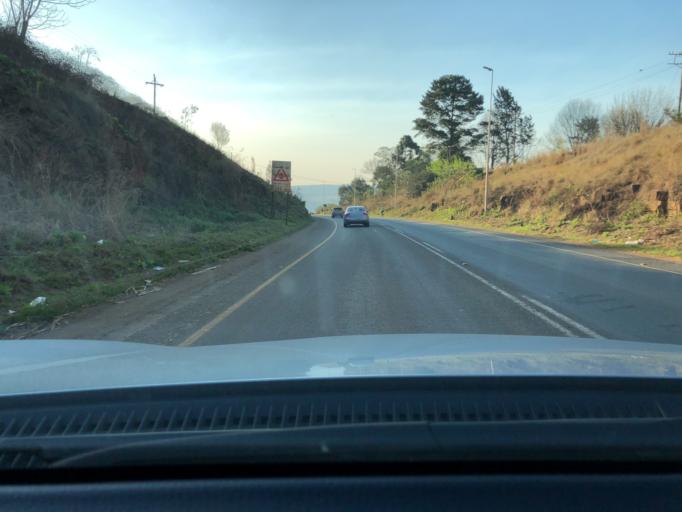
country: ZA
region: KwaZulu-Natal
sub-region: Sisonke District Municipality
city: Ixopo
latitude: -30.1497
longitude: 30.0739
